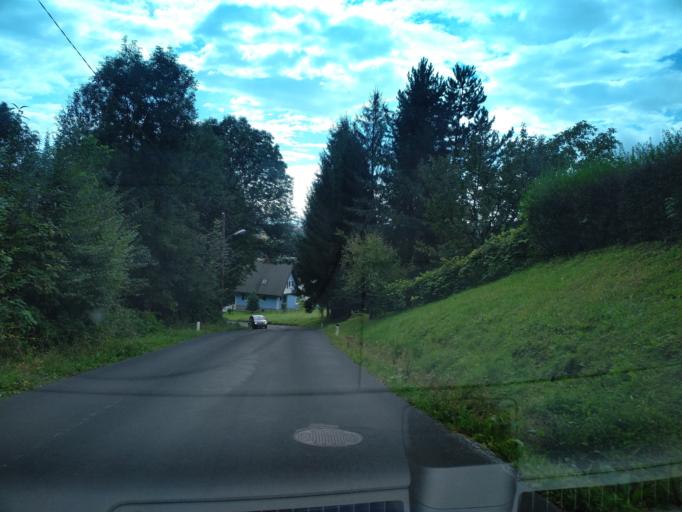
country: AT
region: Styria
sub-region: Politischer Bezirk Deutschlandsberg
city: Deutschlandsberg
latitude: 46.8215
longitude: 15.2075
